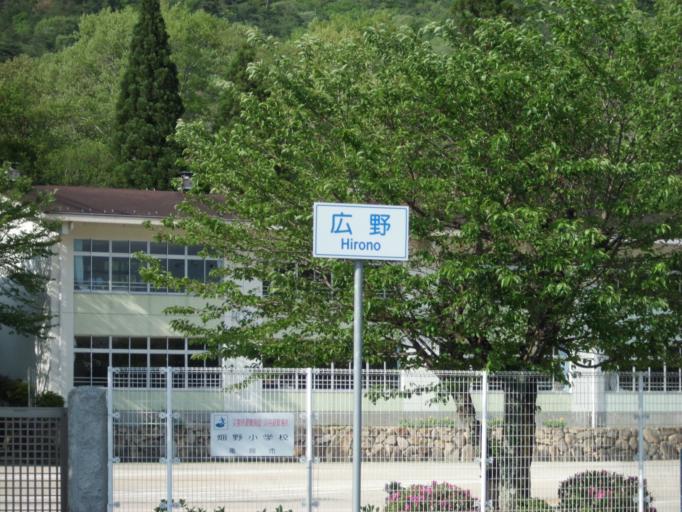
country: JP
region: Kyoto
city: Kameoka
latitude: 35.0143
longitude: 135.4307
